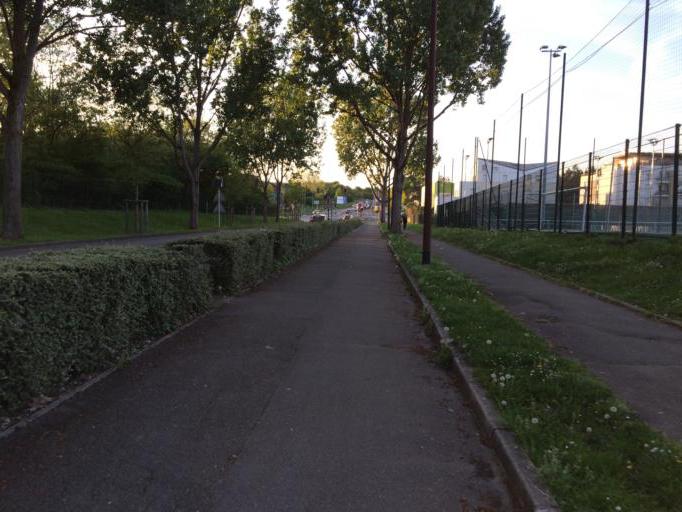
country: FR
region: Ile-de-France
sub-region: Departement de l'Essonne
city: Verrieres-le-Buisson
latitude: 48.7439
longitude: 2.2842
